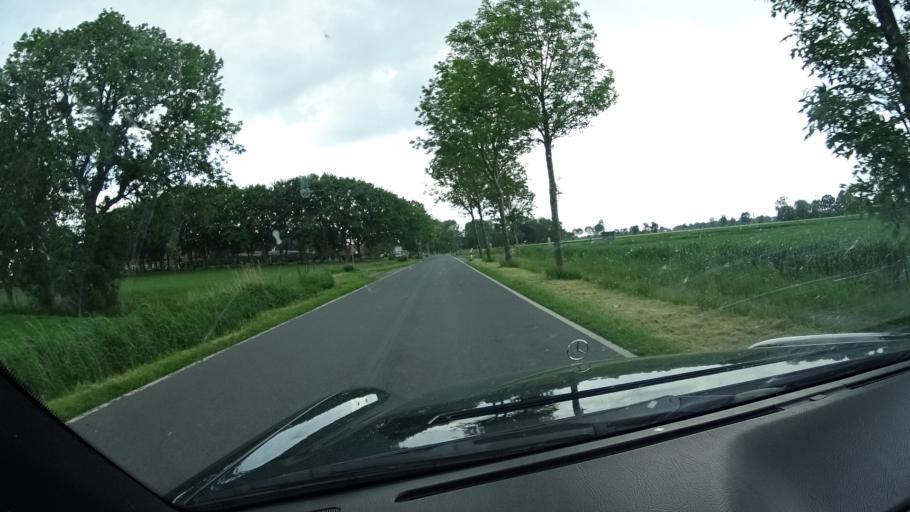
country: DE
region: Lower Saxony
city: Butjadingen
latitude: 53.5839
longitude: 8.2710
